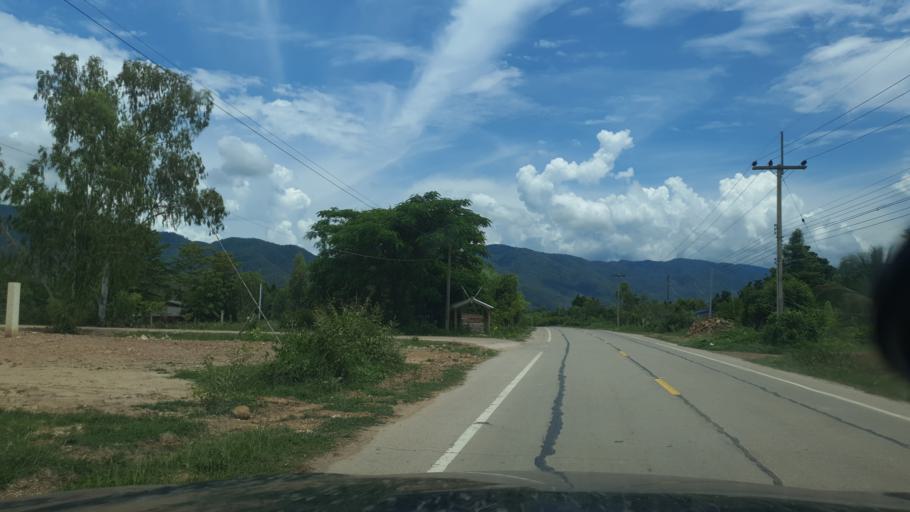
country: TH
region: Lampang
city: Sop Prap
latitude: 17.9184
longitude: 99.4112
